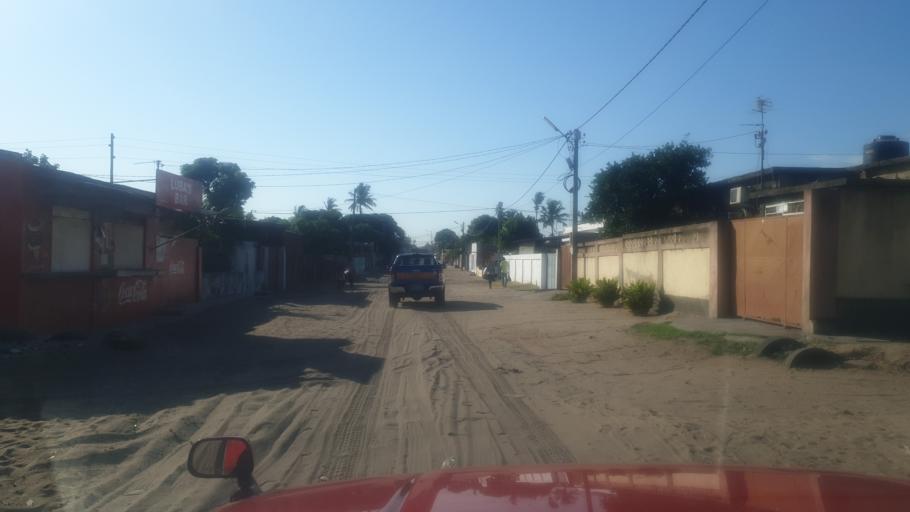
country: MZ
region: Maputo City
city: Maputo
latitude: -25.9124
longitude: 32.5624
